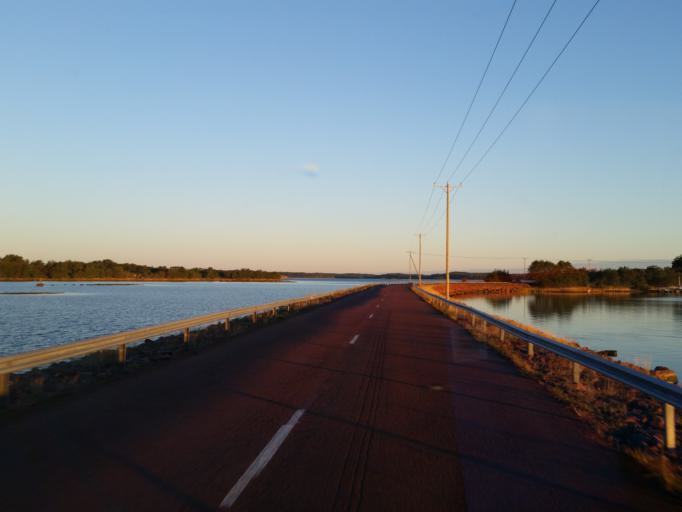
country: AX
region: Alands skaergard
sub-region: Vardoe
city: Vardoe
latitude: 60.3103
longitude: 20.3759
